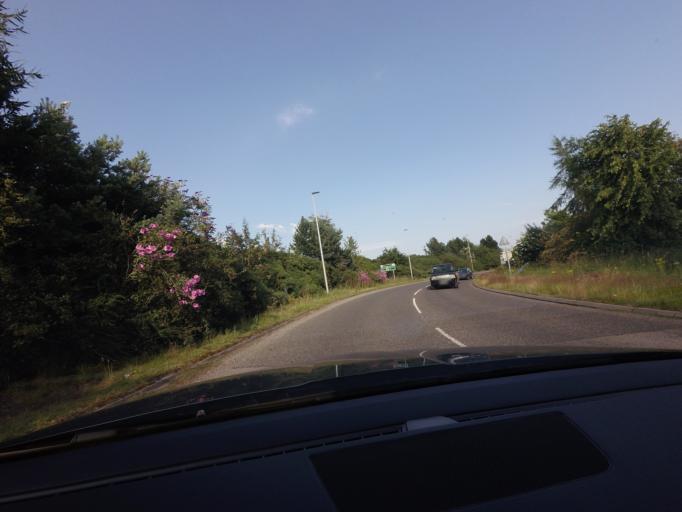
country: GB
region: Scotland
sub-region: Highland
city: Alness
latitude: 57.6918
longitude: -4.2416
